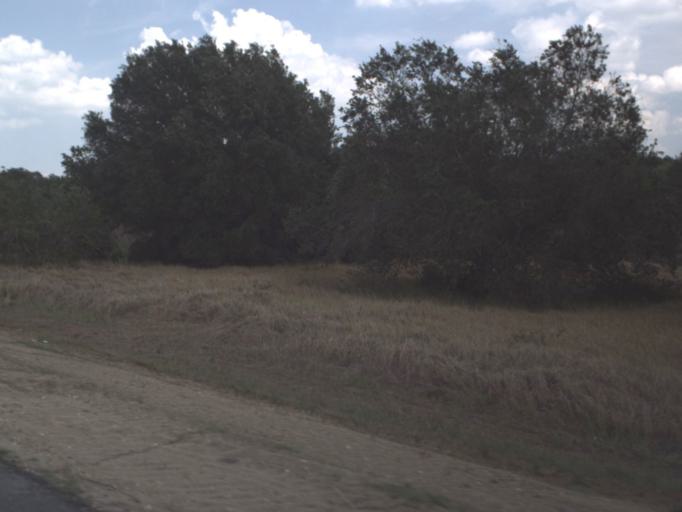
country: US
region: Florida
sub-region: Lake County
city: Groveland
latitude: 28.6328
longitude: -81.8185
